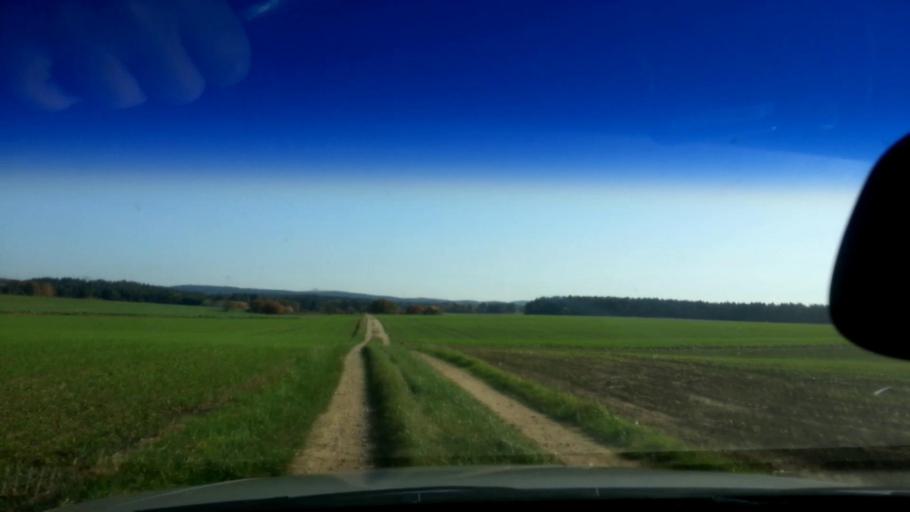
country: DE
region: Bavaria
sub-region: Upper Franconia
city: Wonsees
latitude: 49.9683
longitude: 11.2639
